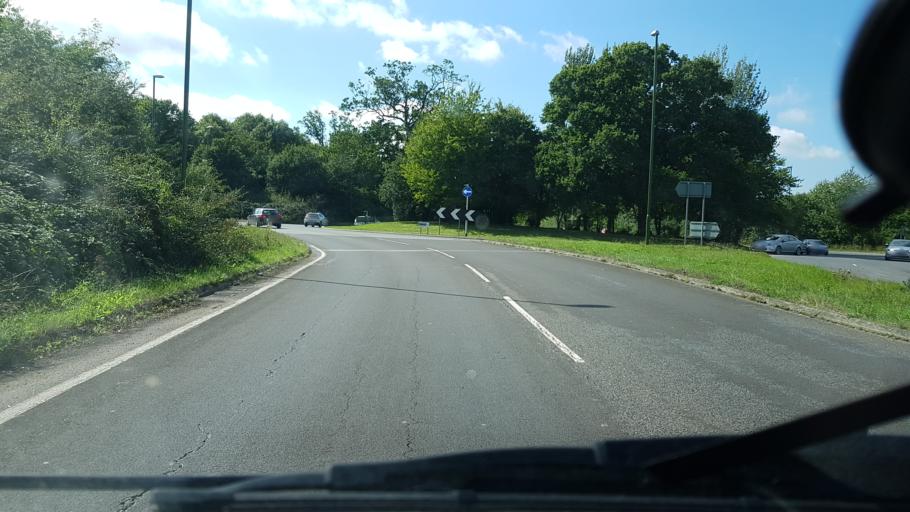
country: GB
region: England
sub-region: West Sussex
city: Horsham
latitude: 51.0876
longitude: -0.3034
